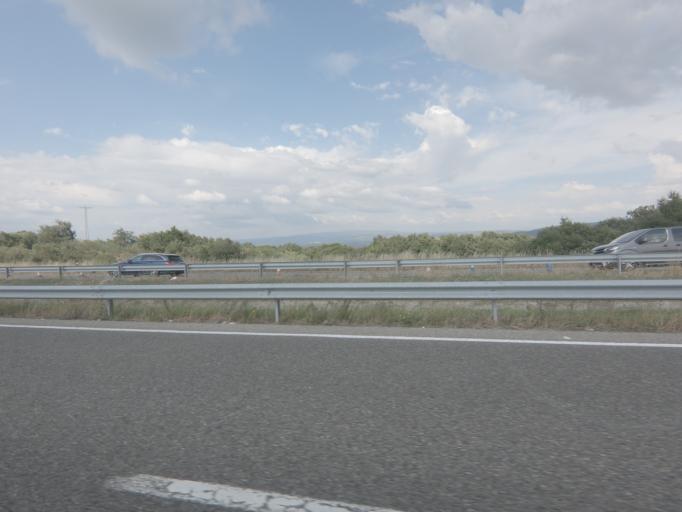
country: ES
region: Galicia
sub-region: Provincia de Ourense
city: Taboadela
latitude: 42.2397
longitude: -7.8588
